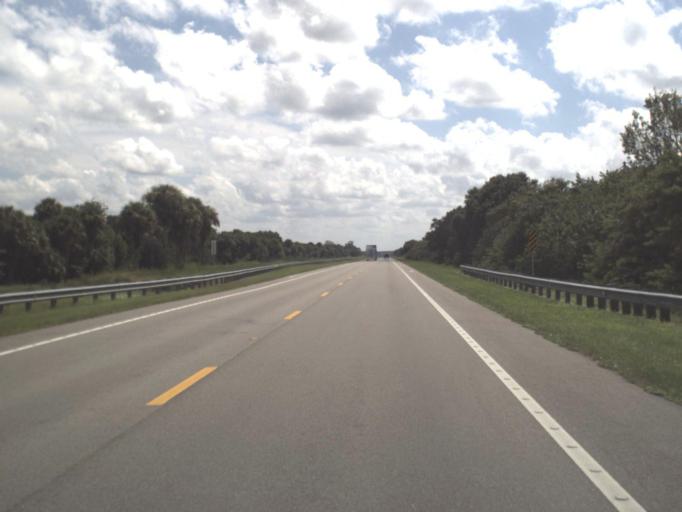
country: US
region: Florida
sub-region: Collier County
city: Immokalee
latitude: 26.3895
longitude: -81.3764
